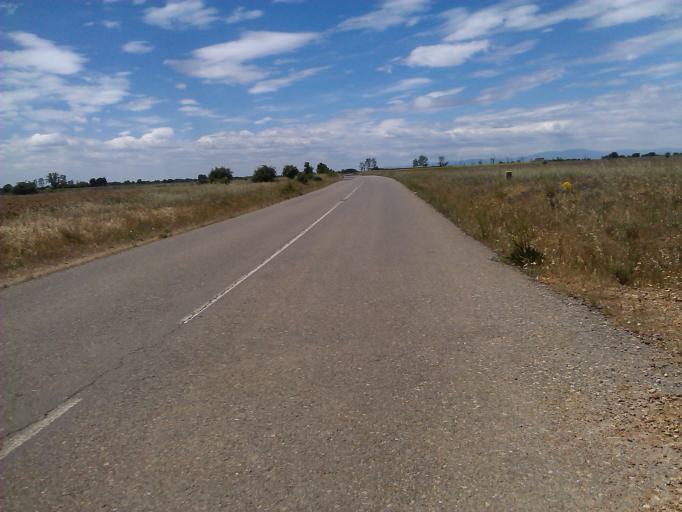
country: ES
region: Castille and Leon
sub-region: Provincia de Leon
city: Chozas de Abajo
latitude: 42.5060
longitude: -5.6920
